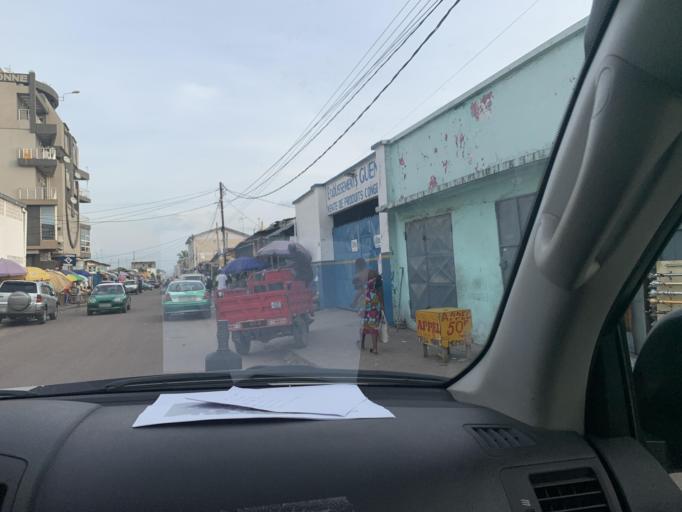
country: CG
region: Brazzaville
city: Brazzaville
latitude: -4.2495
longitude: 15.2843
